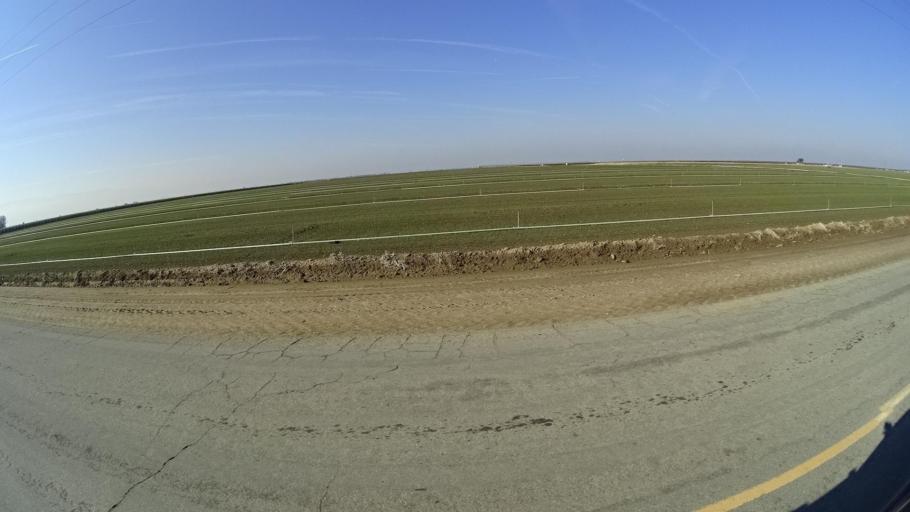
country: US
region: California
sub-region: Kern County
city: Arvin
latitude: 35.1858
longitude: -118.8781
